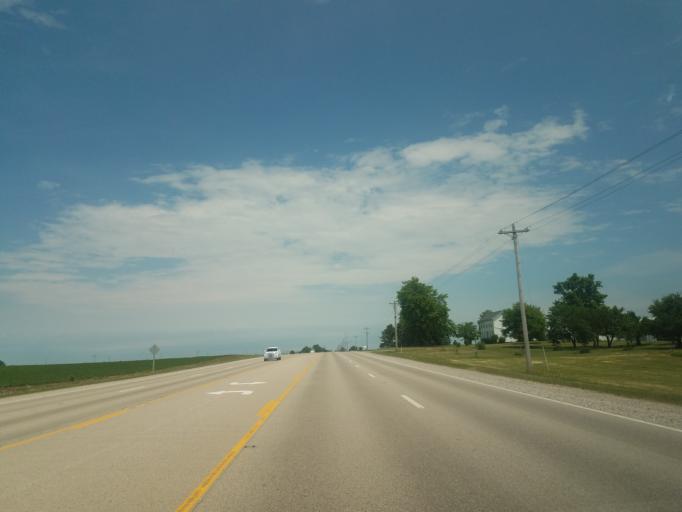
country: US
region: Illinois
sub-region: McLean County
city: Downs
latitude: 40.4276
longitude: -88.9014
